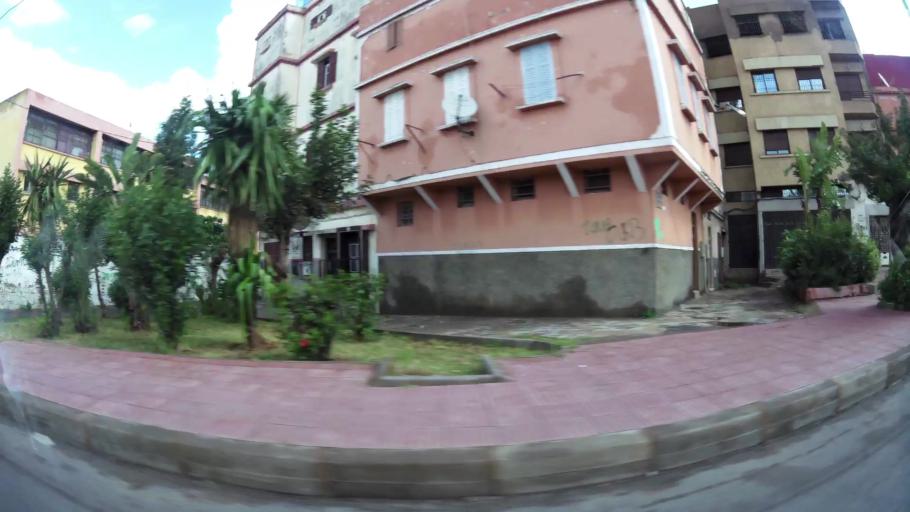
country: MA
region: Grand Casablanca
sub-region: Casablanca
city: Casablanca
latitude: 33.5493
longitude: -7.5938
